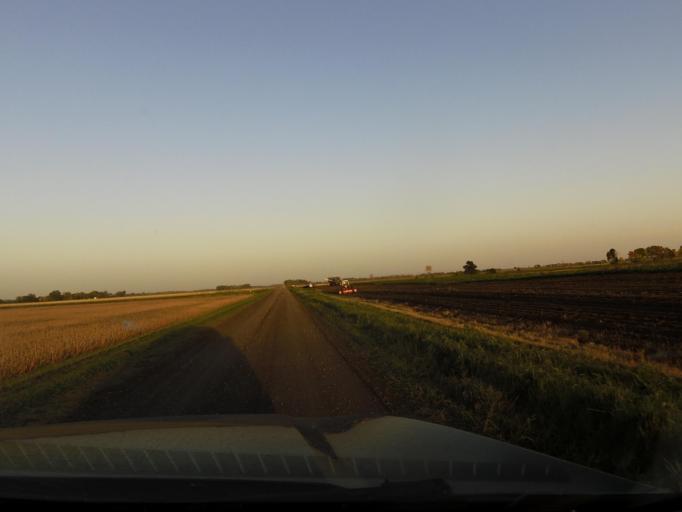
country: US
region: North Dakota
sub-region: Walsh County
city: Grafton
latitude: 48.3832
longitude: -97.2265
